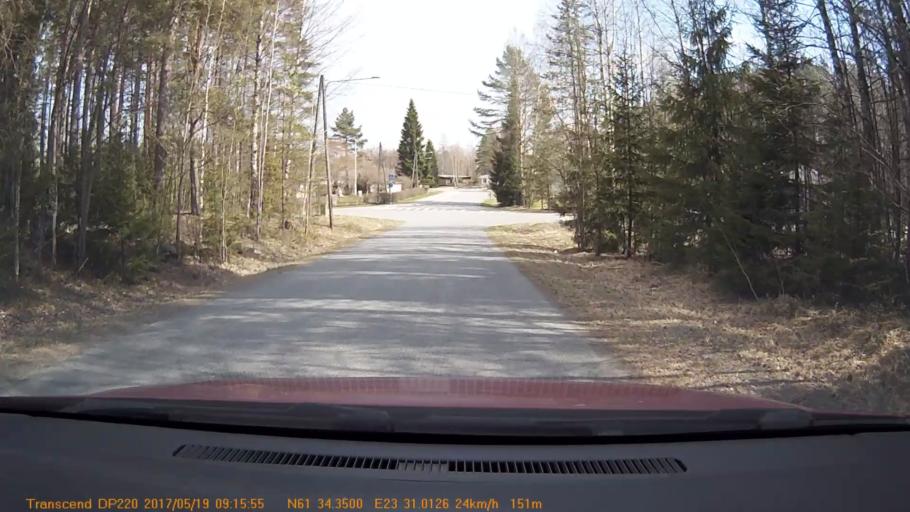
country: FI
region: Pirkanmaa
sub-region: Tampere
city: Yloejaervi
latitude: 61.5725
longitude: 23.5168
